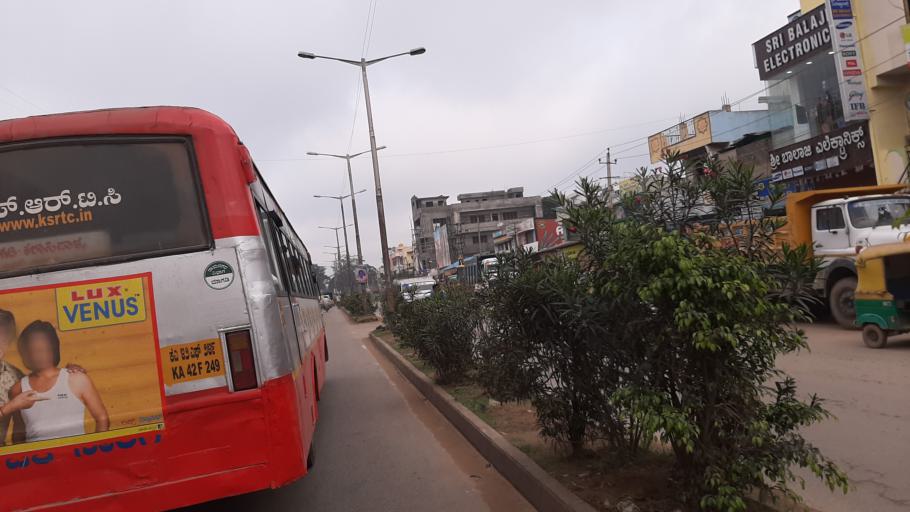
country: IN
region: Karnataka
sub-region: Bangalore Urban
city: Bangalore
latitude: 12.9877
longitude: 77.4748
